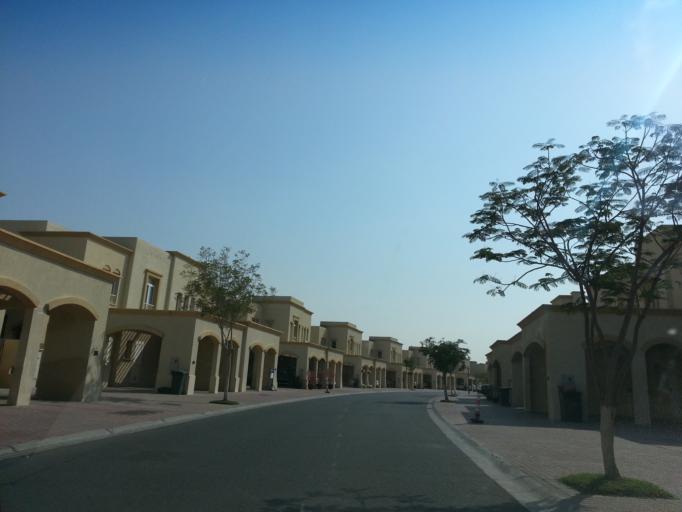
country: AE
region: Dubai
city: Dubai
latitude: 25.0583
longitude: 55.1830
